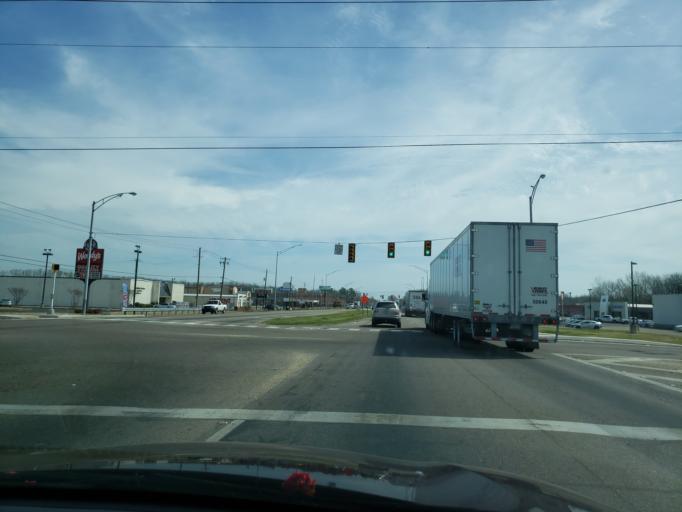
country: US
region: Alabama
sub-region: Dallas County
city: Selma
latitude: 32.4313
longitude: -87.0145
